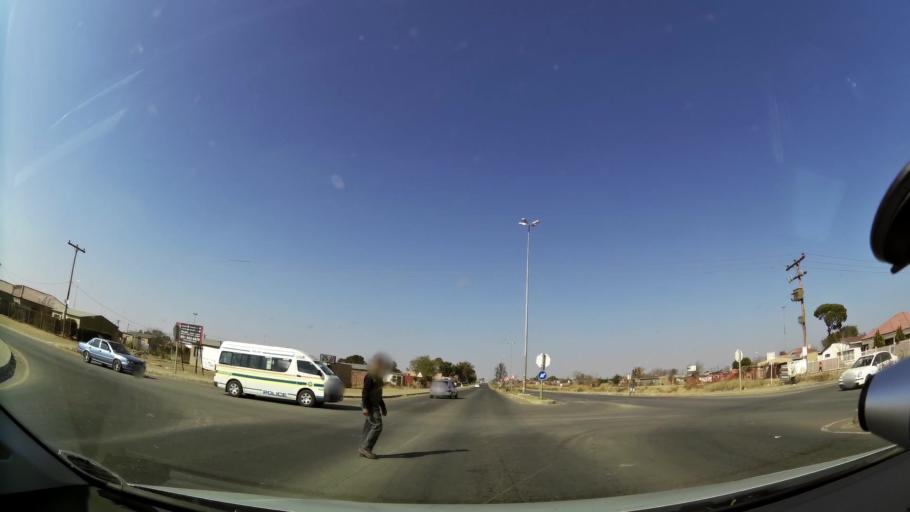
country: ZA
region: Orange Free State
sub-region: Mangaung Metropolitan Municipality
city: Bloemfontein
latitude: -29.1518
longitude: 26.2706
